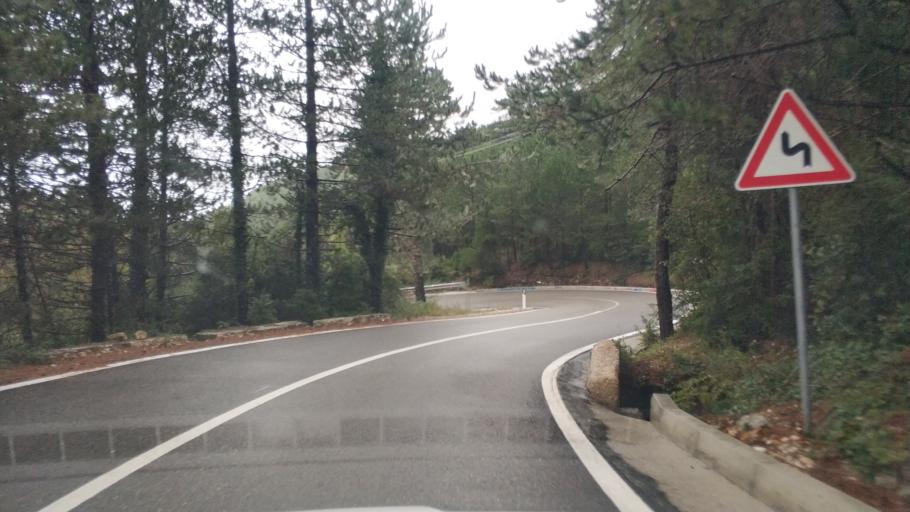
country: AL
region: Vlore
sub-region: Rrethi i Vlores
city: Brataj
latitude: 40.2051
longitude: 19.5861
